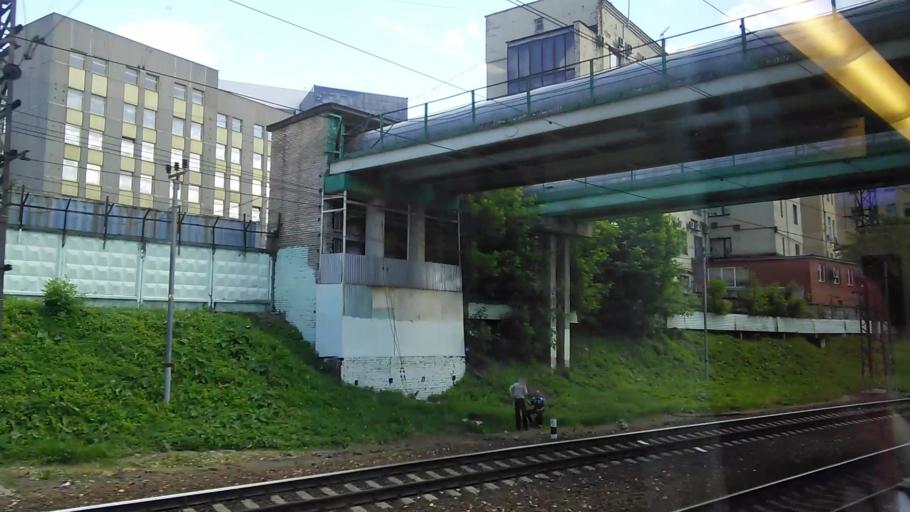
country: RU
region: Moskovskaya
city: Dorogomilovo
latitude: 55.7805
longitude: 37.5858
